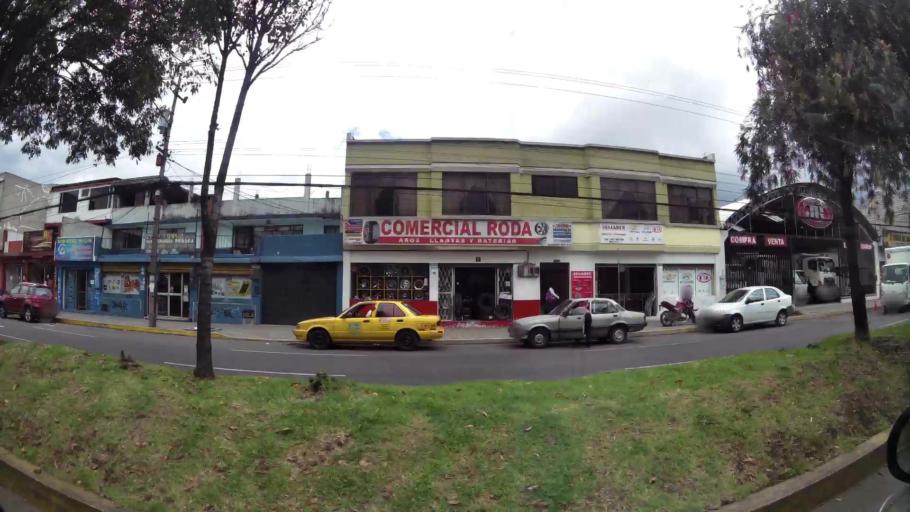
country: EC
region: Pichincha
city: Quito
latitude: -0.2488
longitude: -78.5287
